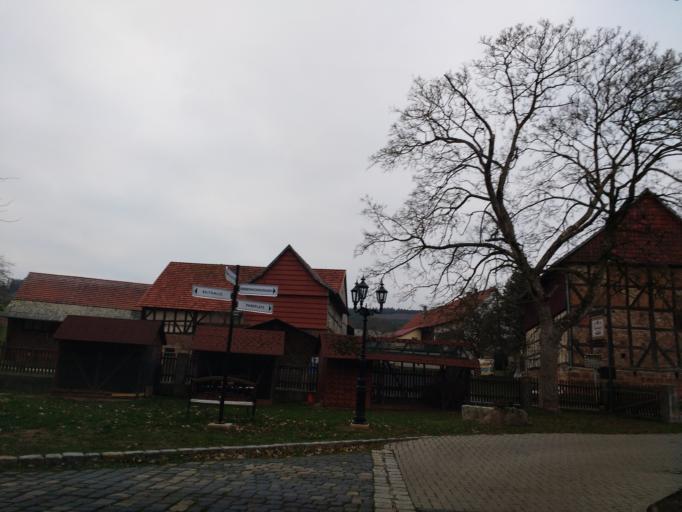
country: DE
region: Hesse
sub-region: Regierungsbezirk Kassel
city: Rotenburg an der Fulda
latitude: 51.0670
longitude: 9.7771
